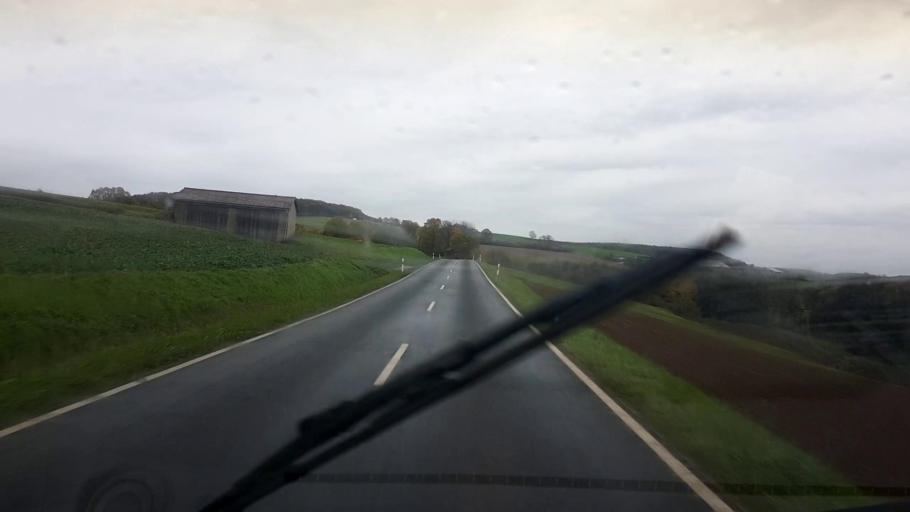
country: DE
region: Bavaria
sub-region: Upper Franconia
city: Burgwindheim
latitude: 49.8800
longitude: 10.5845
